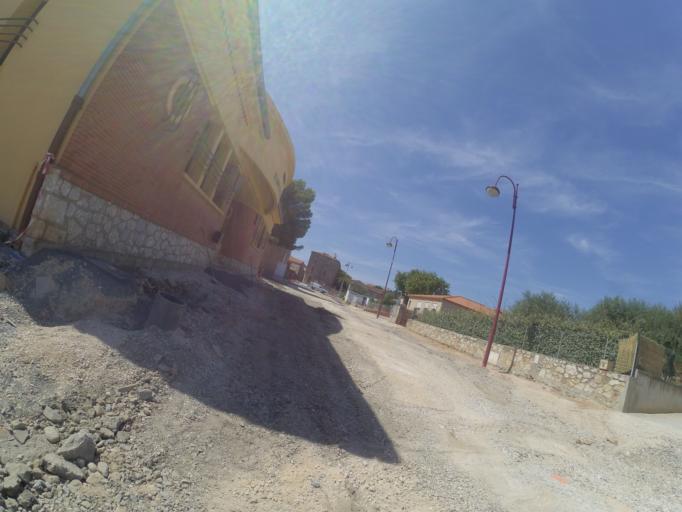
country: FR
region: Languedoc-Roussillon
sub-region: Departement des Pyrenees-Orientales
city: Baixas
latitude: 42.7513
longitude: 2.8126
